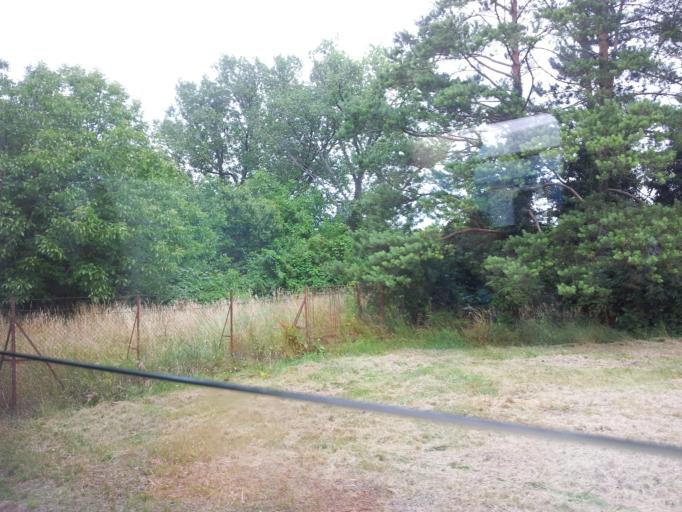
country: HU
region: Veszprem
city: Badacsonytomaj
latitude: 46.8106
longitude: 17.4695
